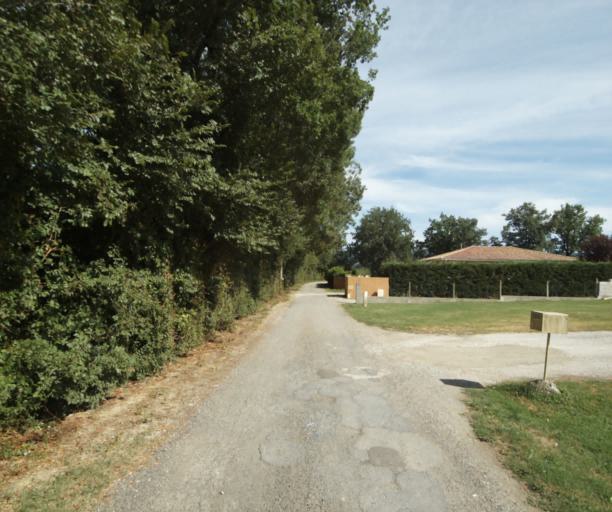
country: FR
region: Midi-Pyrenees
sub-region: Departement du Tarn
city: Soual
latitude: 43.5223
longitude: 2.0960
